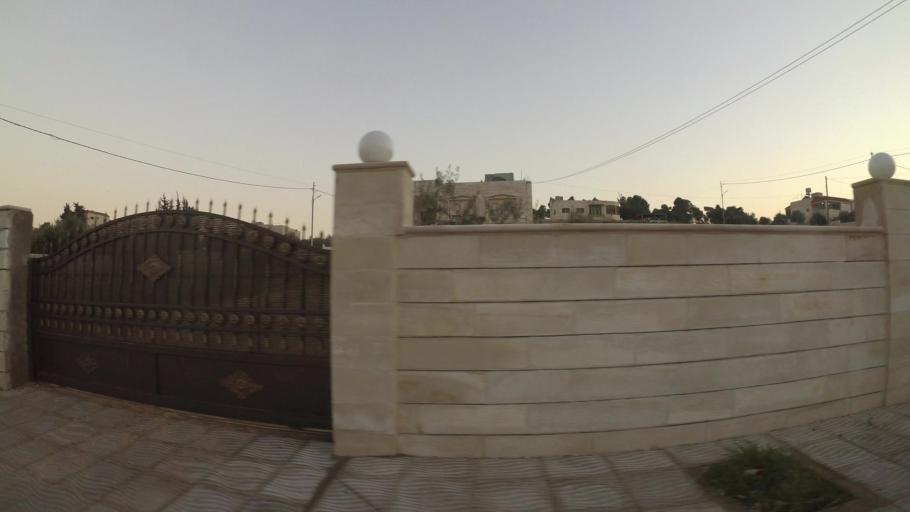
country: JO
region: Amman
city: Al Bunayyat ash Shamaliyah
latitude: 31.8933
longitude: 35.9211
